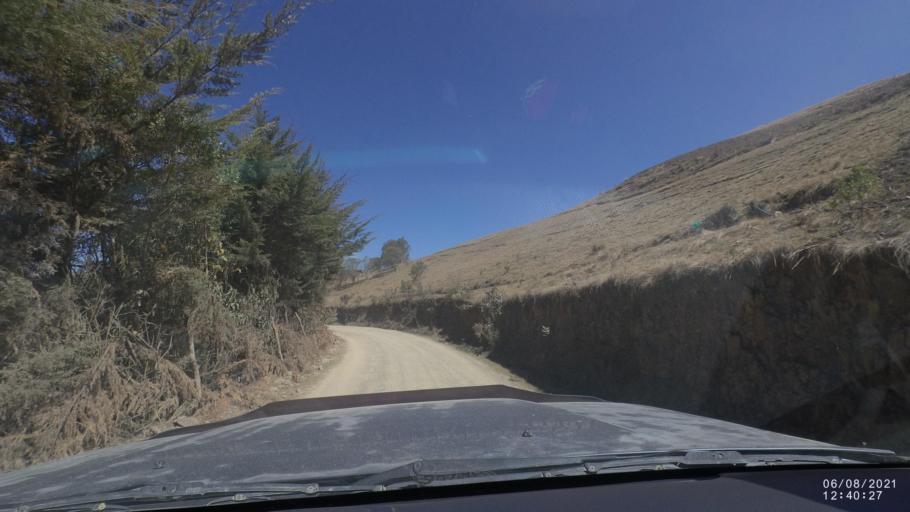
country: BO
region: Cochabamba
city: Colchani
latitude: -16.7838
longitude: -66.6645
